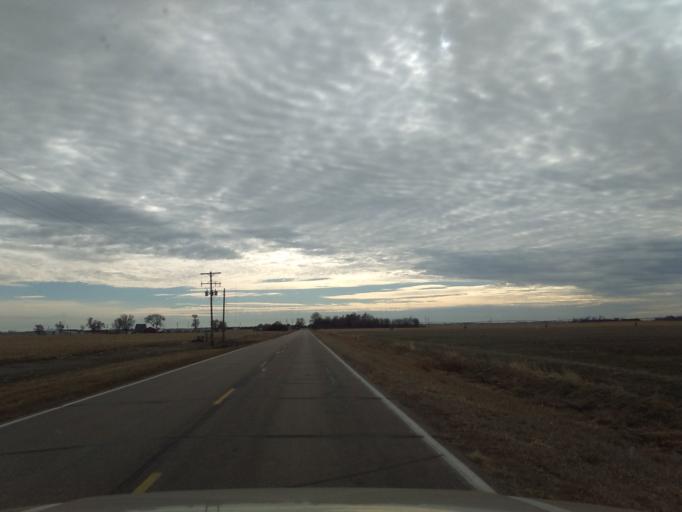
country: US
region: Nebraska
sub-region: Buffalo County
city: Gibbon
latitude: 40.6539
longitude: -98.8473
